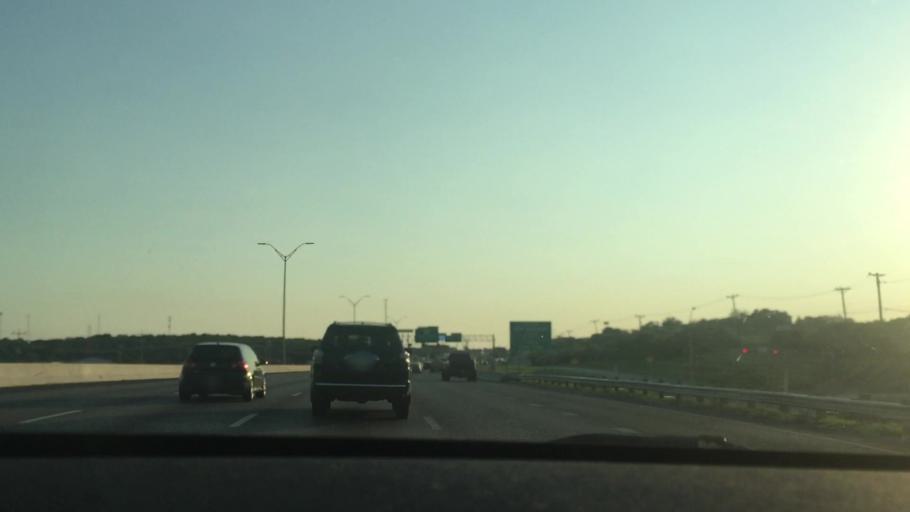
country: US
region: Texas
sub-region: Bexar County
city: Live Oak
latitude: 29.5560
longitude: -98.3475
